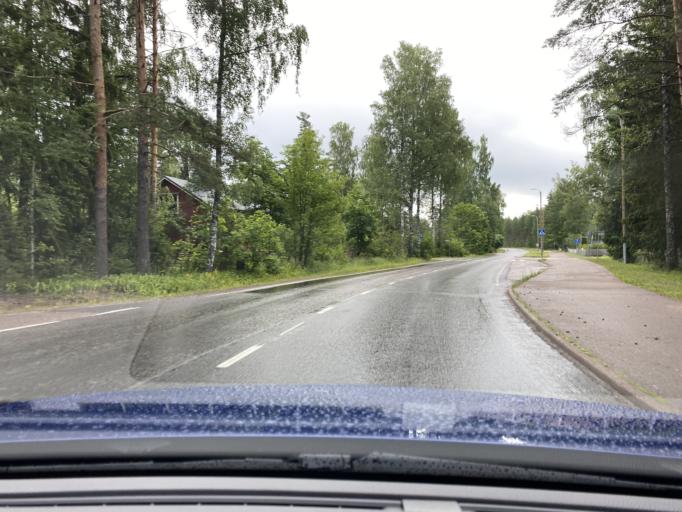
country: FI
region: Uusimaa
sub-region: Helsinki
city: Nurmijaervi
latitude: 60.5723
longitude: 24.7643
